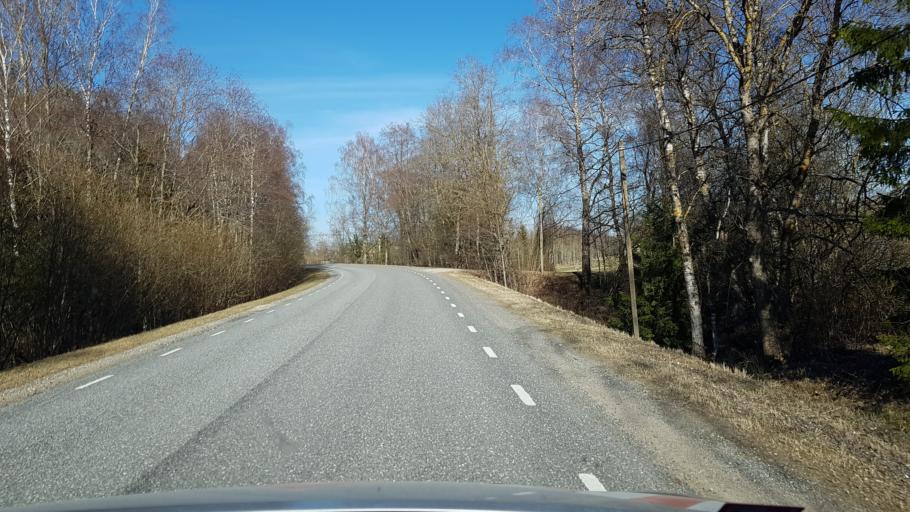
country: EE
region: Laeaene-Virumaa
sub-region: Rakke vald
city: Rakke
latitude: 58.9884
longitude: 26.2661
